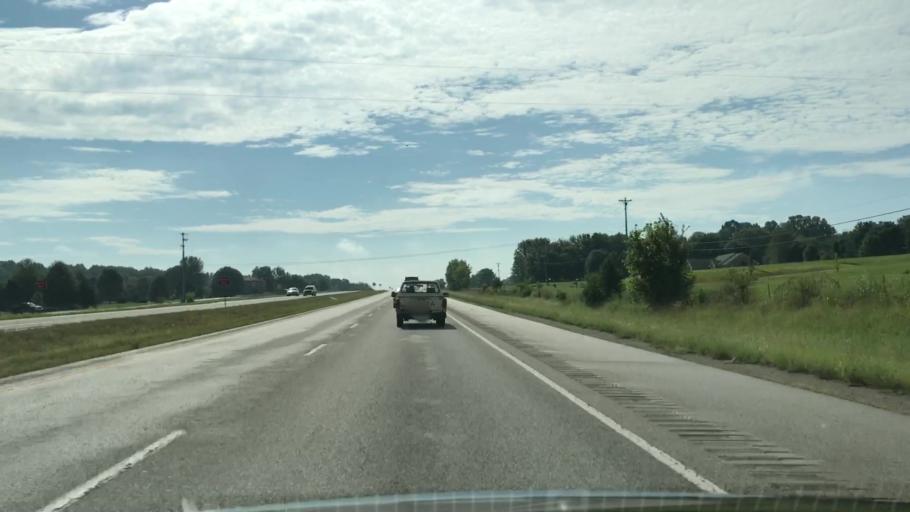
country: US
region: Kentucky
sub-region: Warren County
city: Plano
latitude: 36.8933
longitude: -86.3773
